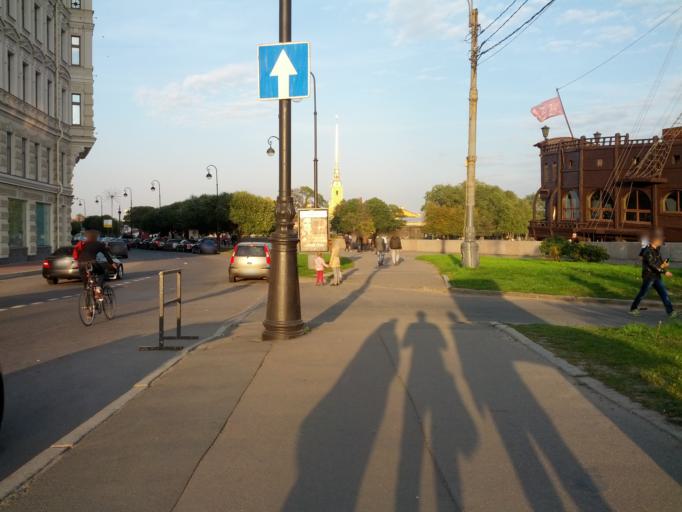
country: RU
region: St.-Petersburg
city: Saint Petersburg
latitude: 59.9480
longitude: 30.3049
